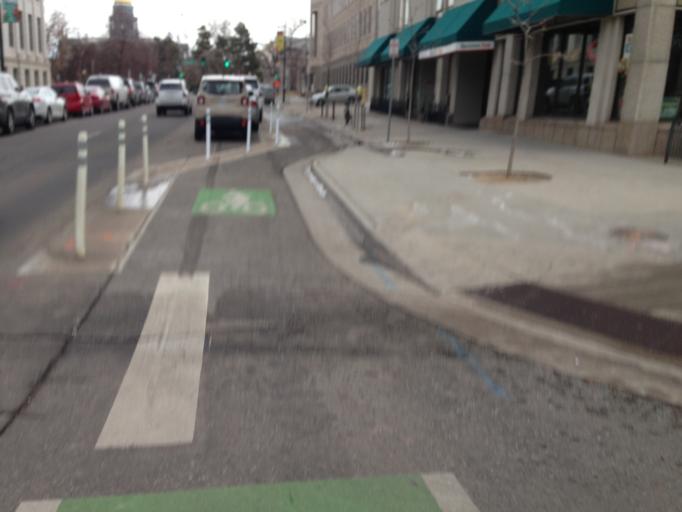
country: US
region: Colorado
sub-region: Denver County
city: Denver
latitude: 39.7384
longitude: -104.9916
